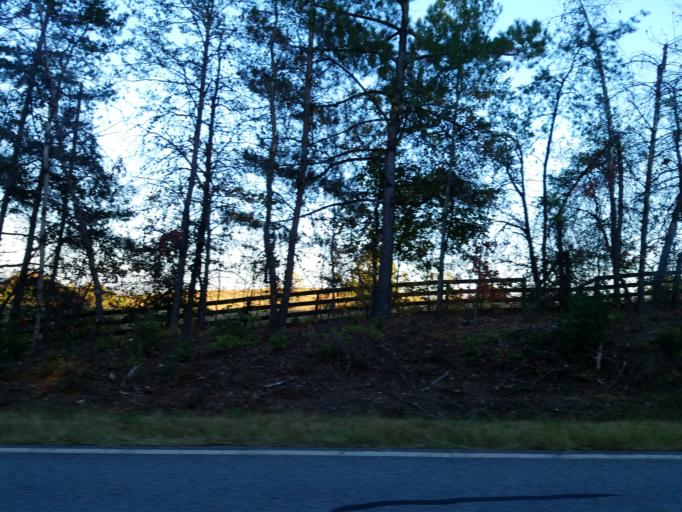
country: US
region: Georgia
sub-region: Lumpkin County
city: Dahlonega
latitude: 34.5304
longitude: -84.0575
